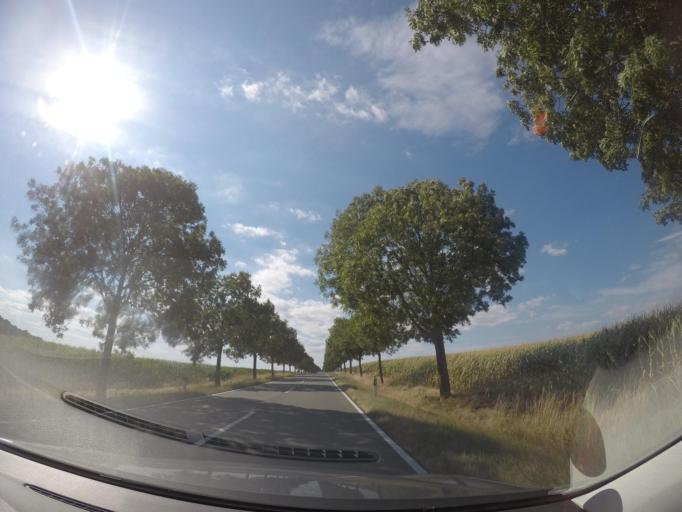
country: DE
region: Saxony-Anhalt
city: Langeln
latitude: 51.9392
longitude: 10.8140
